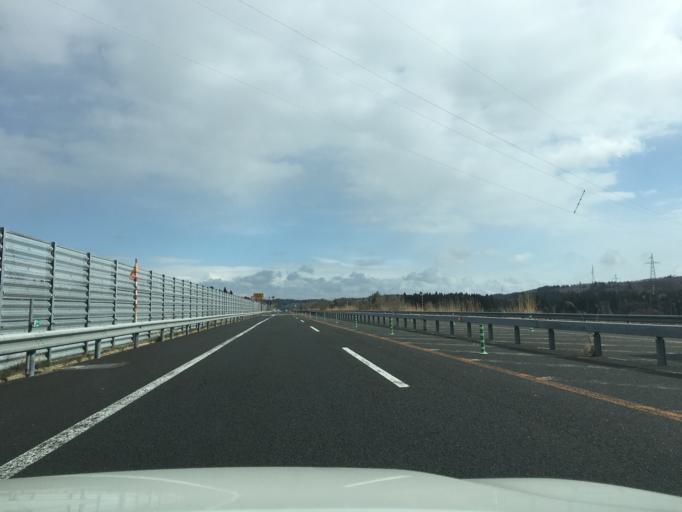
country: JP
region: Akita
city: Akita
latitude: 39.6169
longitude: 140.1459
